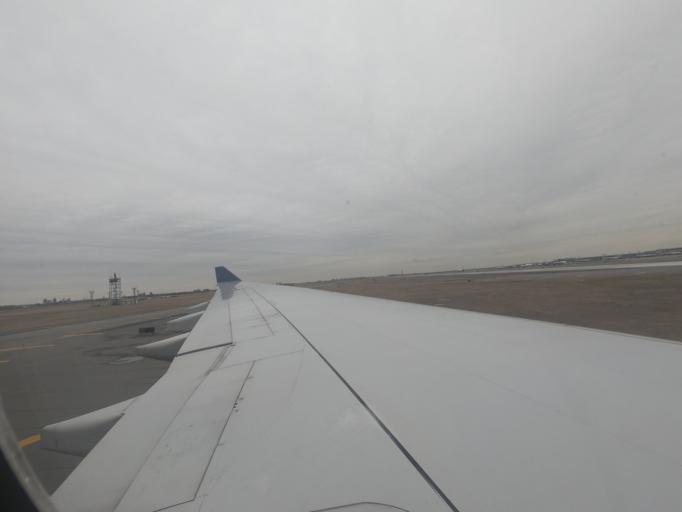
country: US
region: New York
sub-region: Nassau County
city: Inwood
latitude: 40.6429
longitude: -73.7669
